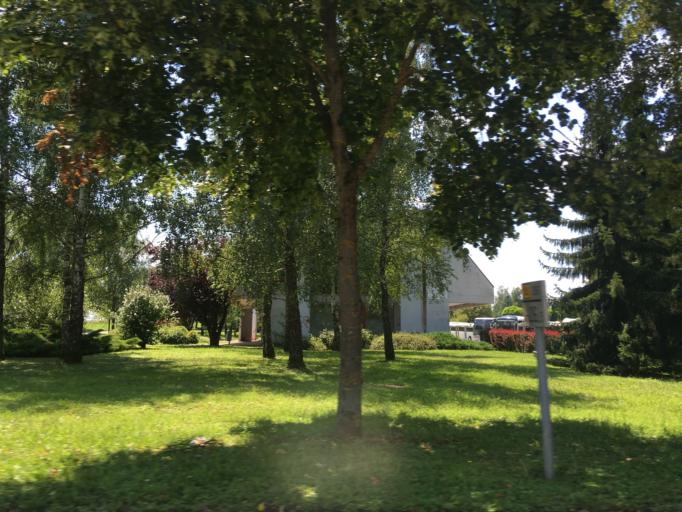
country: SI
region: Metlika
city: Metlika
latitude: 45.6467
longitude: 15.3161
